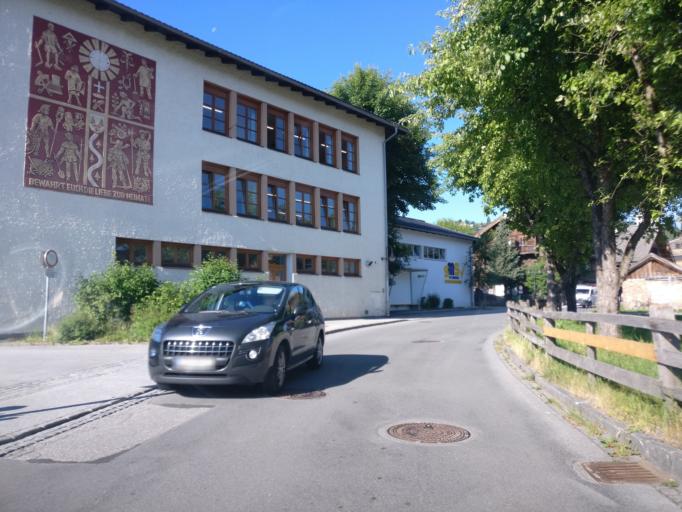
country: AT
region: Salzburg
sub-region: Politischer Bezirk Sankt Johann im Pongau
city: Altenmarkt im Pongau
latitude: 47.3783
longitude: 13.4267
